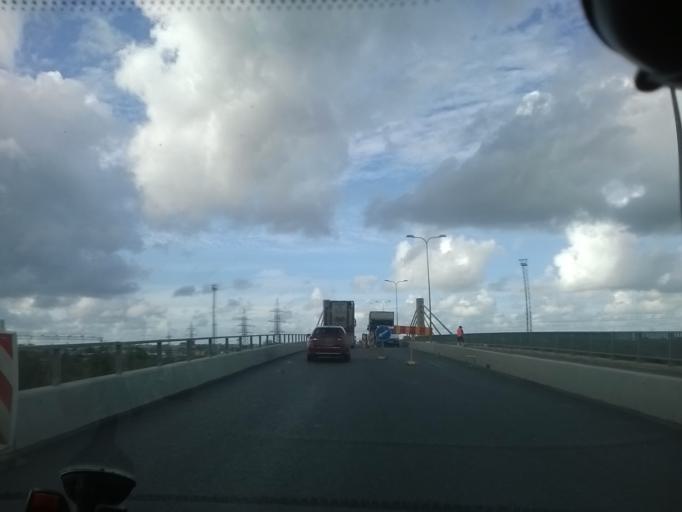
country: EE
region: Harju
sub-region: Tallinna linn
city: Kose
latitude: 59.4204
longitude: 24.8423
